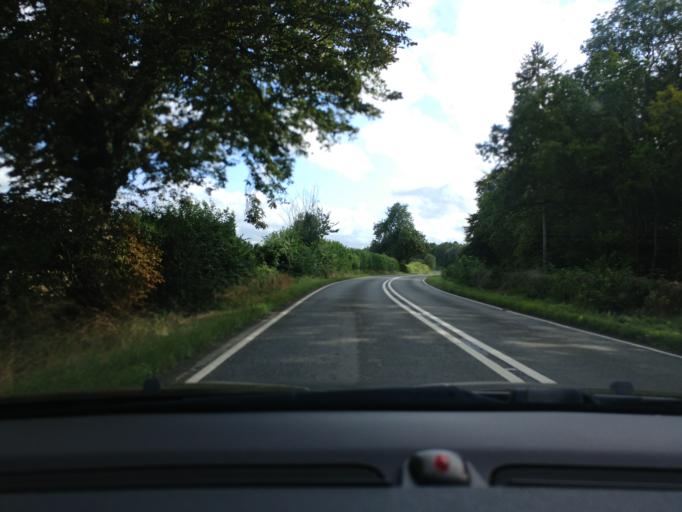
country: GB
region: England
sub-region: Oxfordshire
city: Bicester
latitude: 51.9021
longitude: -1.2250
